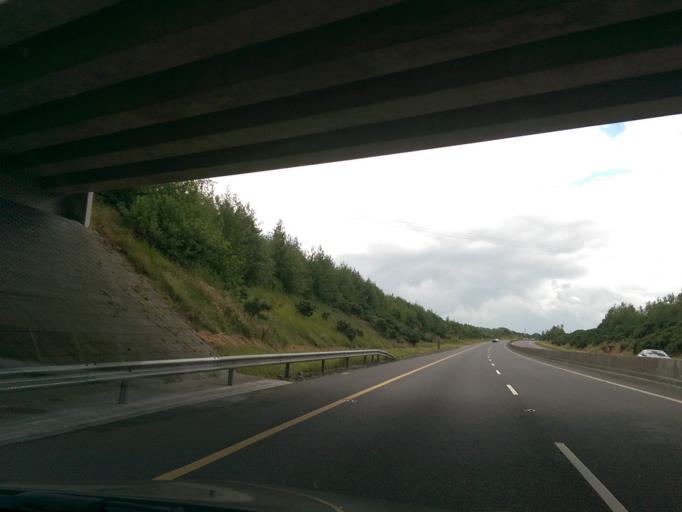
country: IE
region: Munster
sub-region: County Cork
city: Mitchelstown
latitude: 52.2565
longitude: -8.2536
